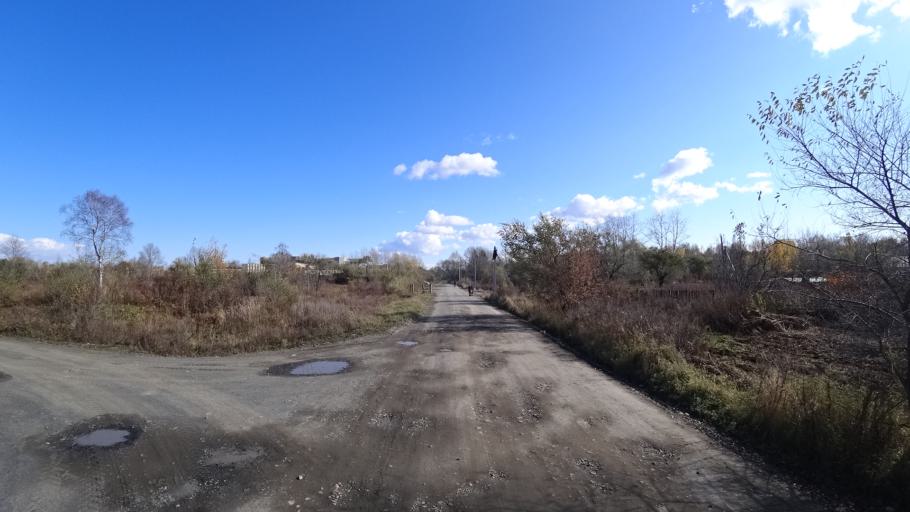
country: RU
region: Khabarovsk Krai
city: Amursk
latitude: 50.1021
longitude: 136.5020
